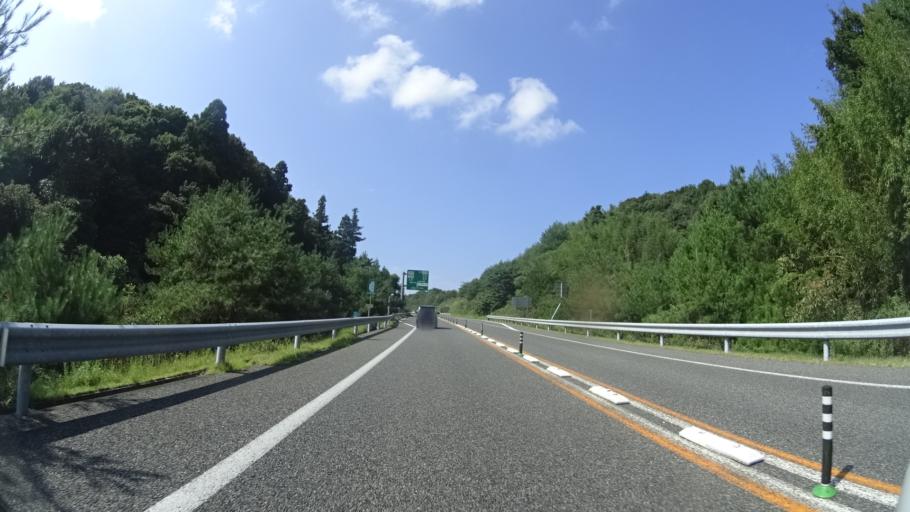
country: JP
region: Shimane
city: Hamada
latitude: 34.9161
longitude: 132.1285
